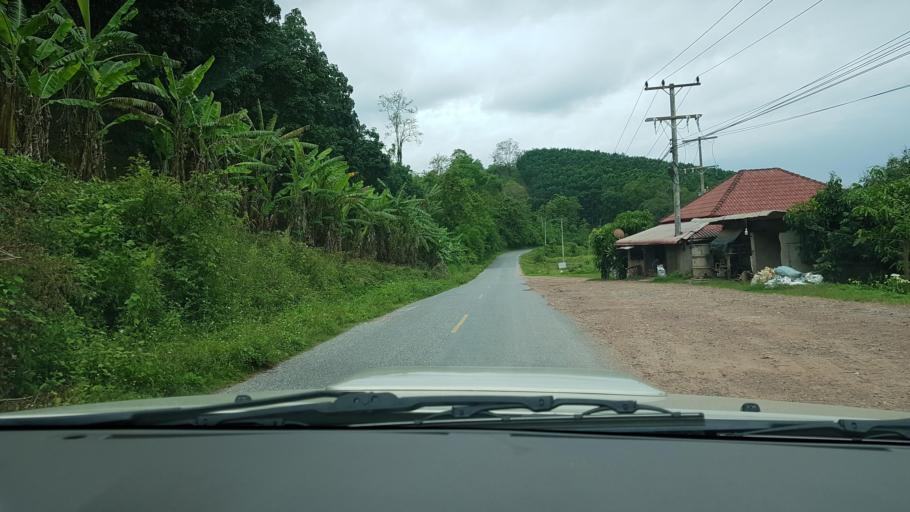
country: LA
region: Loungnamtha
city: Muang Nale
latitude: 20.3887
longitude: 101.7468
